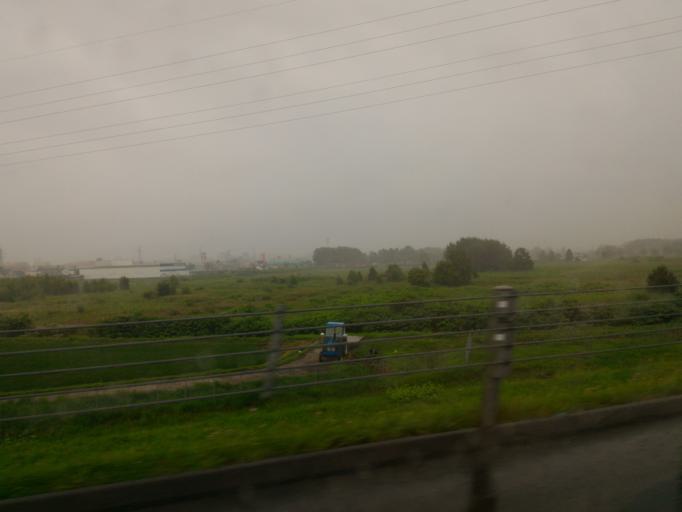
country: JP
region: Hokkaido
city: Nayoro
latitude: 44.3338
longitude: 142.4450
